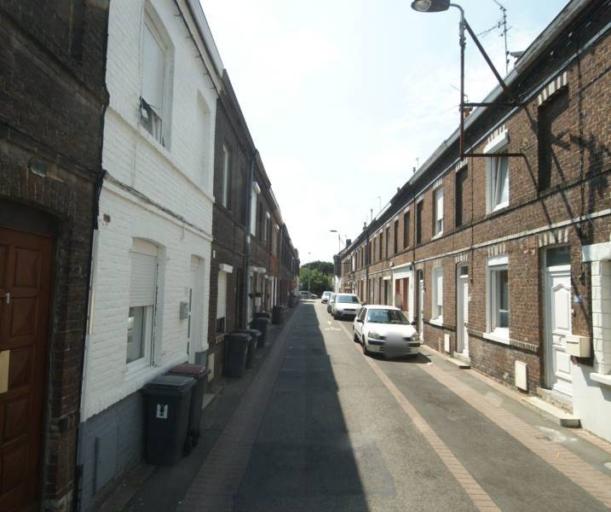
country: FR
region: Nord-Pas-de-Calais
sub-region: Departement du Nord
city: Saint-Andre-lez-Lille
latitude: 50.6592
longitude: 3.0529
